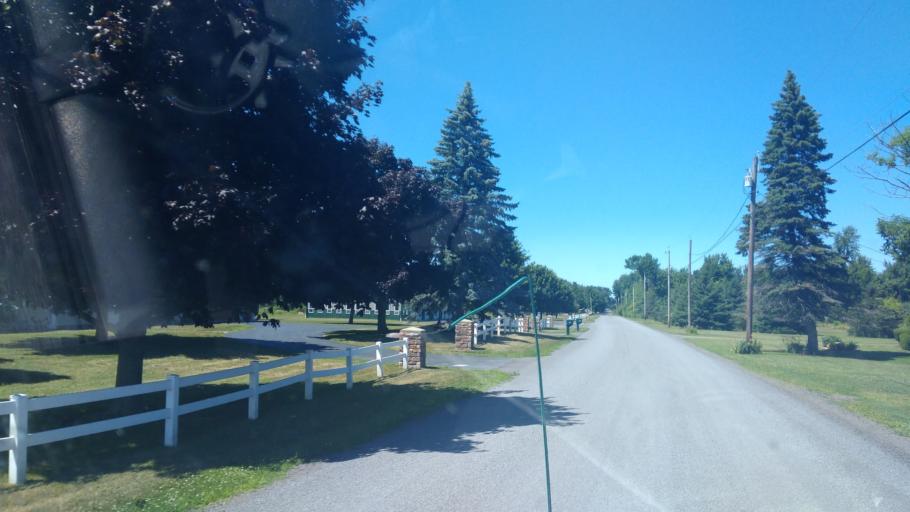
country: US
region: New York
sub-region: Wayne County
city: Sodus
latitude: 43.1757
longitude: -76.9779
